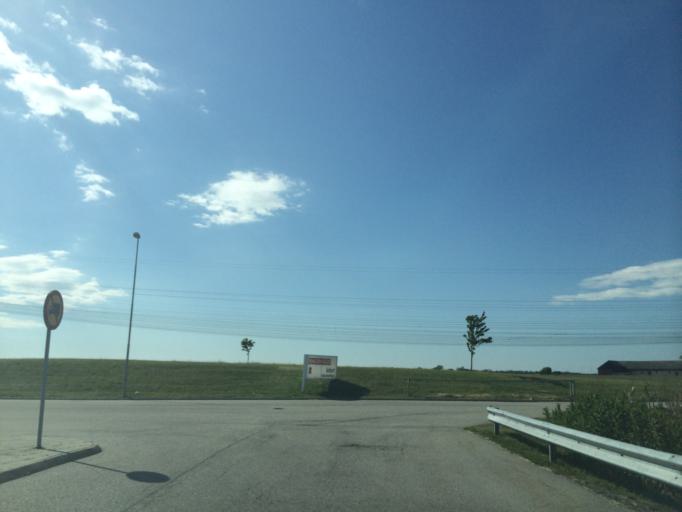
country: SE
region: Skane
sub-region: Kavlinge Kommun
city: Hofterup
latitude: 55.7715
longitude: 12.9849
